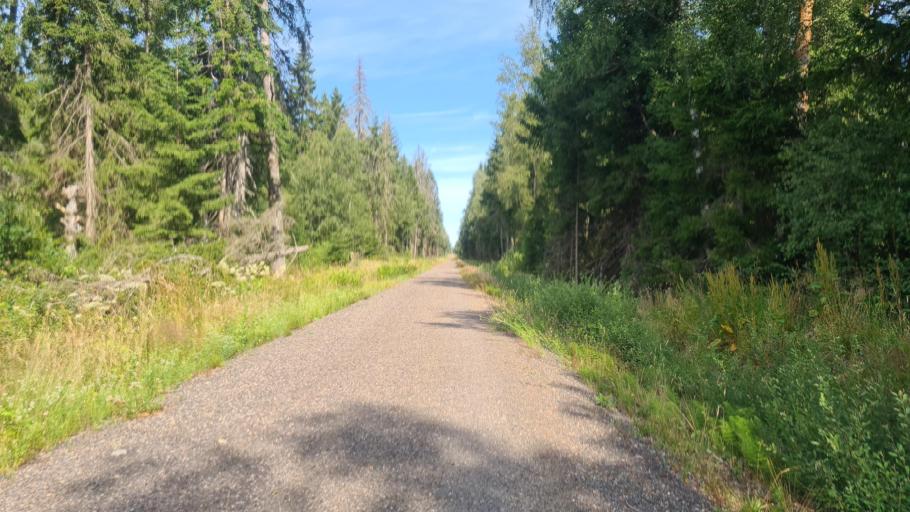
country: SE
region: Kronoberg
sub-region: Ljungby Kommun
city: Lagan
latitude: 56.9748
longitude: 13.9488
